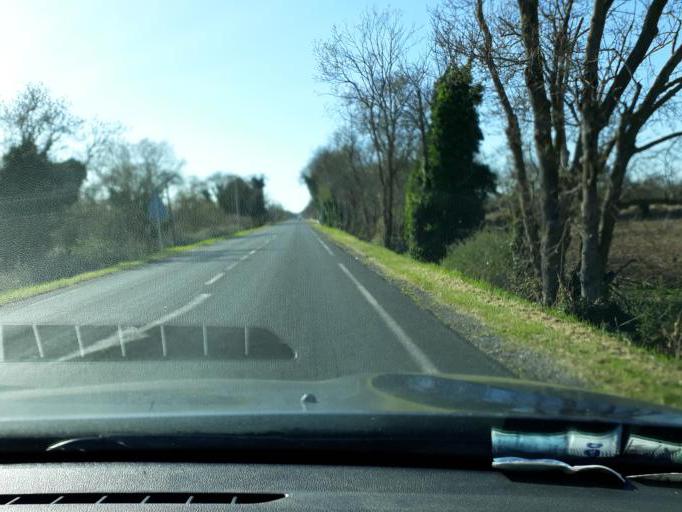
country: FR
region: Languedoc-Roussillon
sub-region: Departement de l'Herault
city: Agde
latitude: 43.3145
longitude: 3.4611
